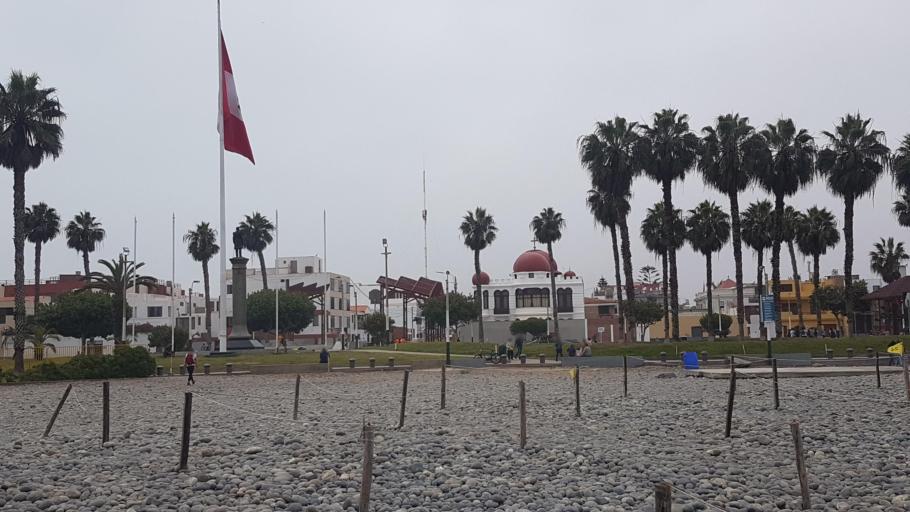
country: PE
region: Callao
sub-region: Callao
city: Callao
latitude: -12.0739
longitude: -77.1661
